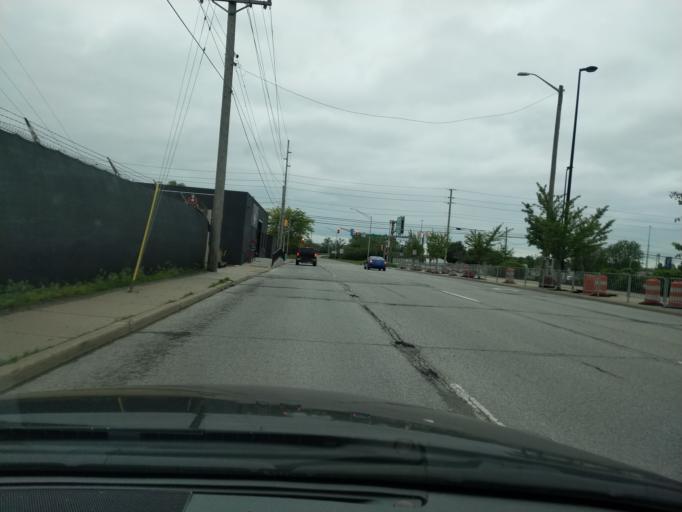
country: US
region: Indiana
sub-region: Marion County
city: Indianapolis
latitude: 39.7574
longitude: -86.1621
